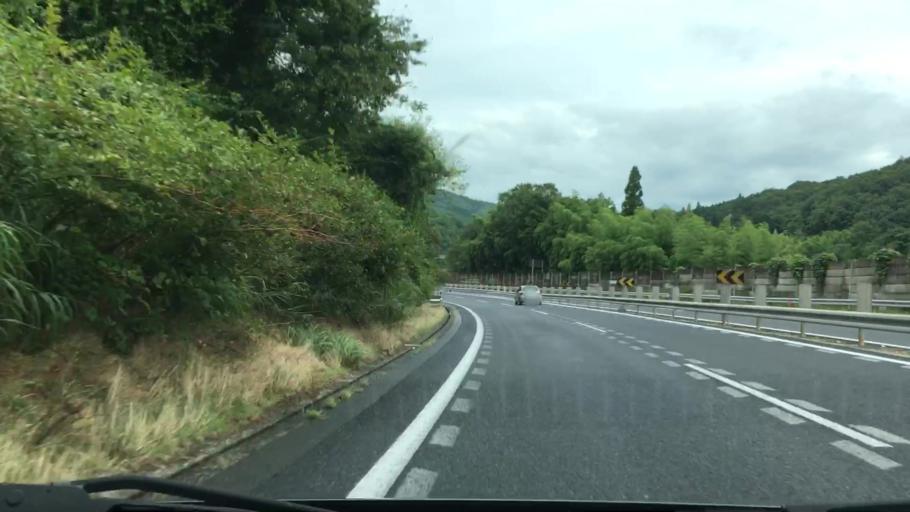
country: JP
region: Hyogo
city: Yamazakicho-nakabirose
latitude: 35.0078
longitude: 134.3280
